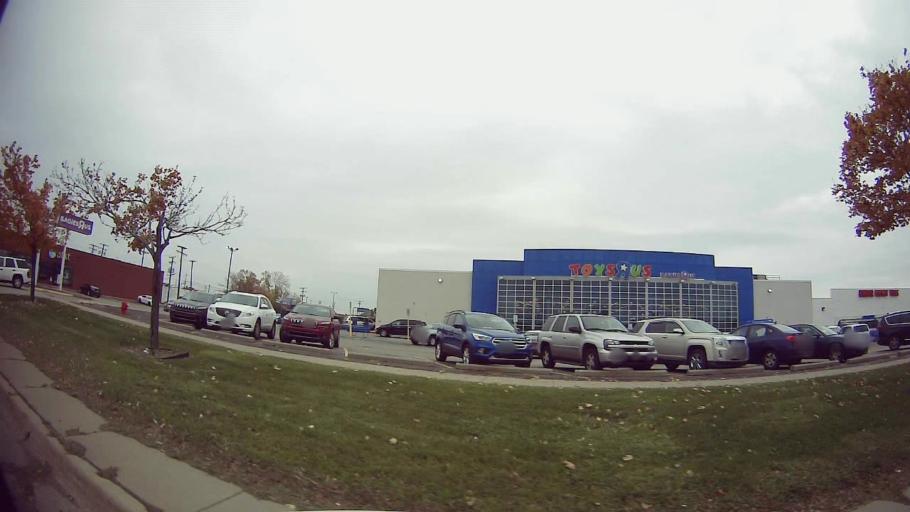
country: US
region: Michigan
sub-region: Oakland County
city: Clawson
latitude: 42.5326
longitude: -83.1068
